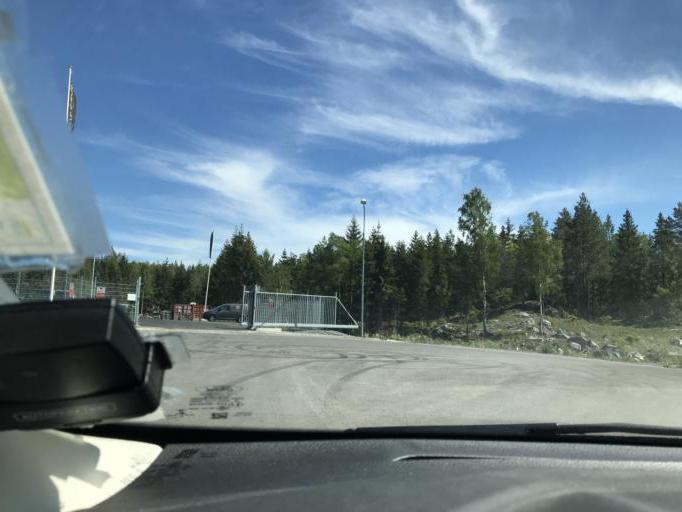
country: SE
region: Stockholm
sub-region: Botkyrka Kommun
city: Alby
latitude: 59.2138
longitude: 17.8490
